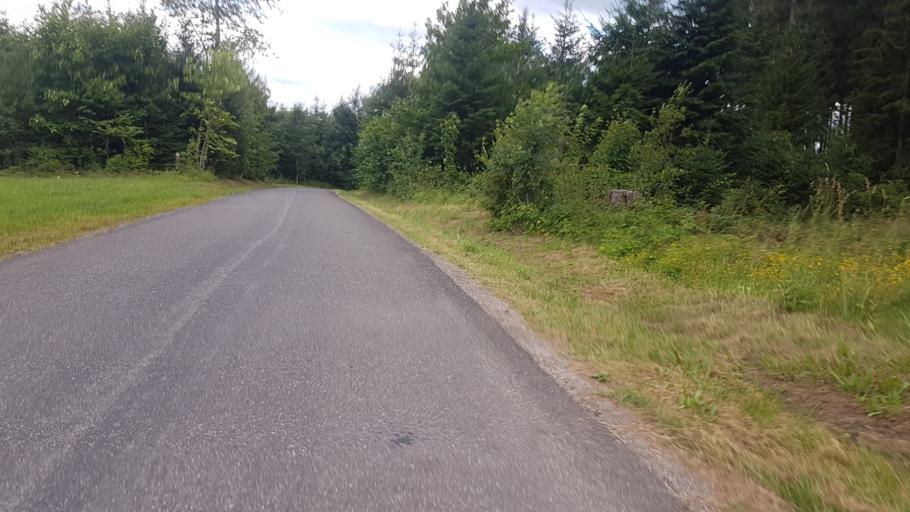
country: DE
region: Baden-Wuerttemberg
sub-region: Freiburg Region
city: Unterkirnach
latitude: 48.0217
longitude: 8.4054
